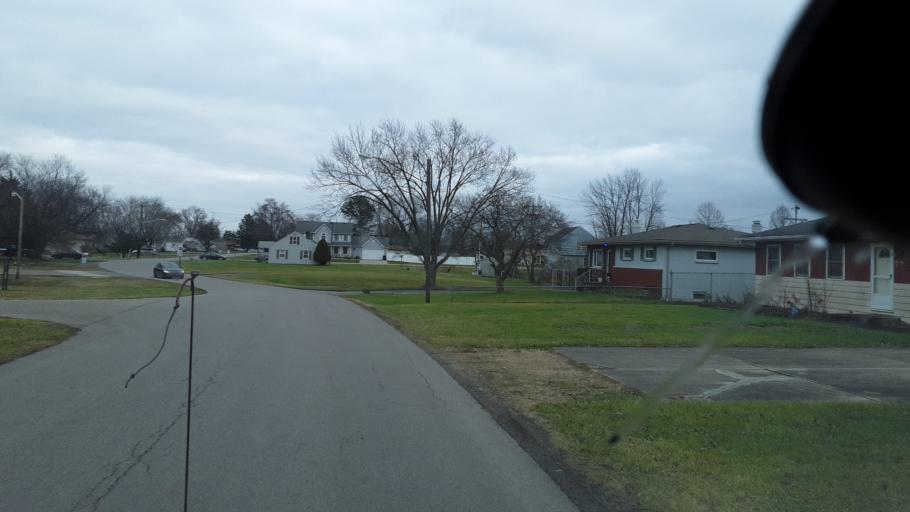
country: US
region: Ohio
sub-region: Franklin County
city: Obetz
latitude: 39.8767
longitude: -82.9373
